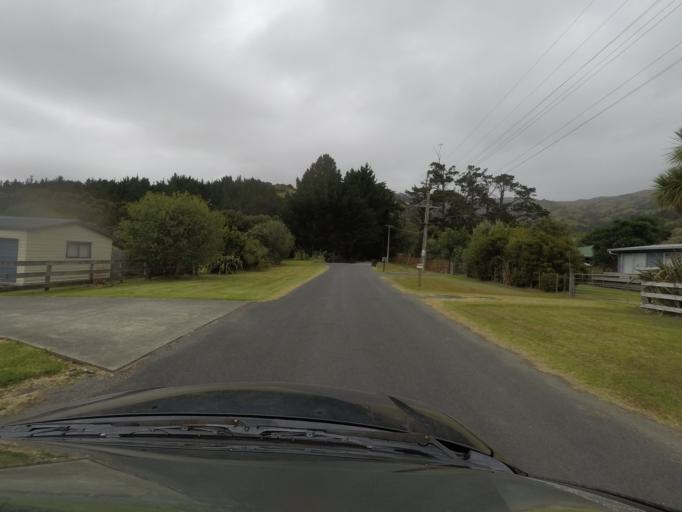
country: NZ
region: Auckland
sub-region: Auckland
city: Warkworth
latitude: -36.2657
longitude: 174.7279
